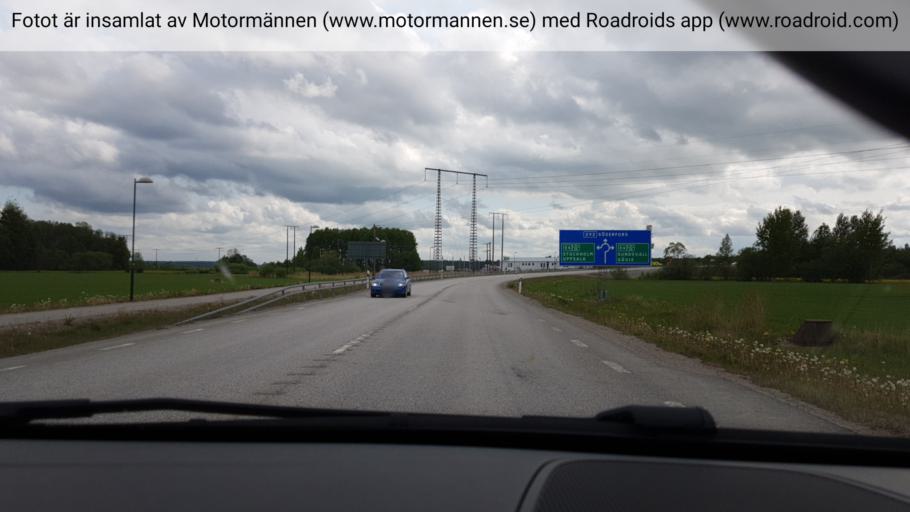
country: SE
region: Uppsala
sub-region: Tierps Kommun
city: Tierp
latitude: 60.3435
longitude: 17.4894
